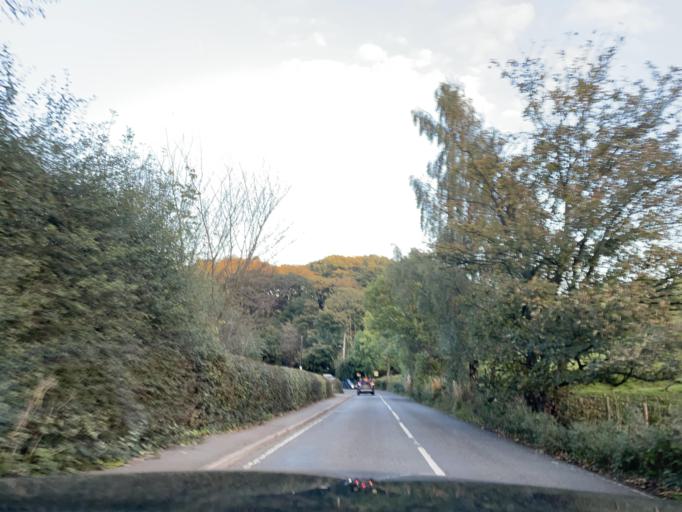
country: GB
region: England
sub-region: Borough of Tameside
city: Longdendale
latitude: 53.4259
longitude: -2.0141
